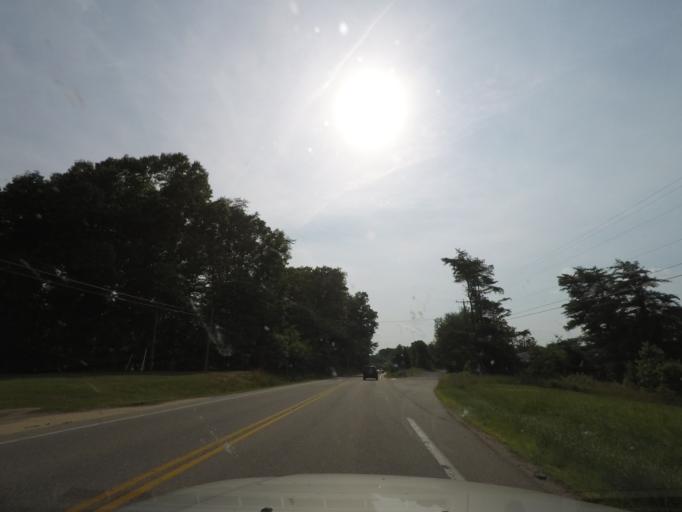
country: US
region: Virginia
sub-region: Prince Edward County
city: Hampden Sydney
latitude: 37.2523
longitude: -78.4266
